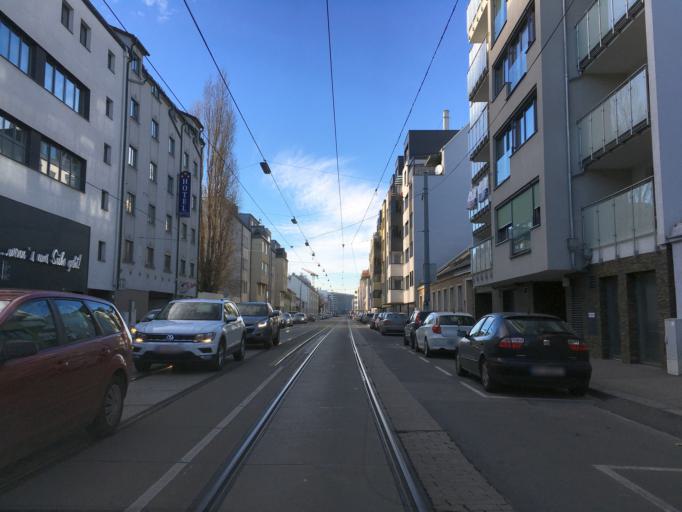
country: AT
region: Lower Austria
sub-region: Politischer Bezirk Wien-Umgebung
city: Gerasdorf bei Wien
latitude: 48.2502
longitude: 16.4402
